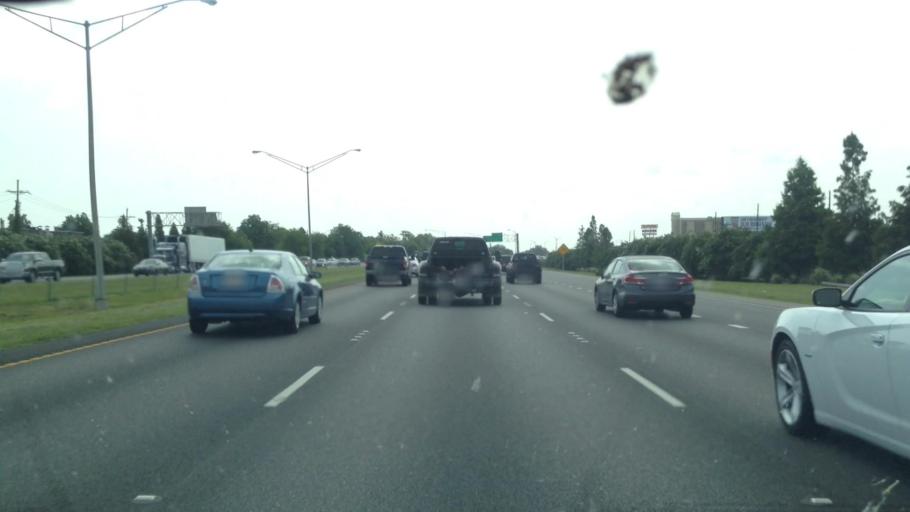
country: US
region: Louisiana
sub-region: Jefferson Parish
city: Kenner
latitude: 30.0077
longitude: -90.2166
